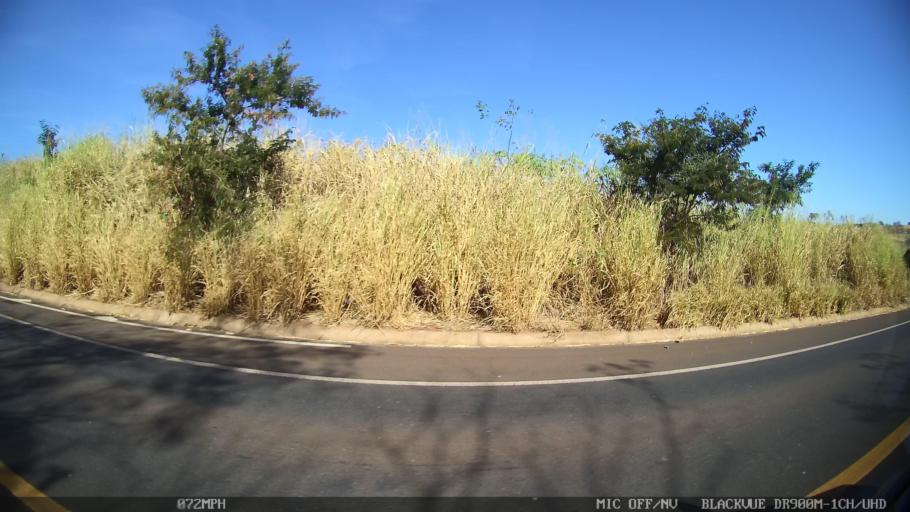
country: BR
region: Sao Paulo
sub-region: Barretos
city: Barretos
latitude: -20.6027
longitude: -48.7318
